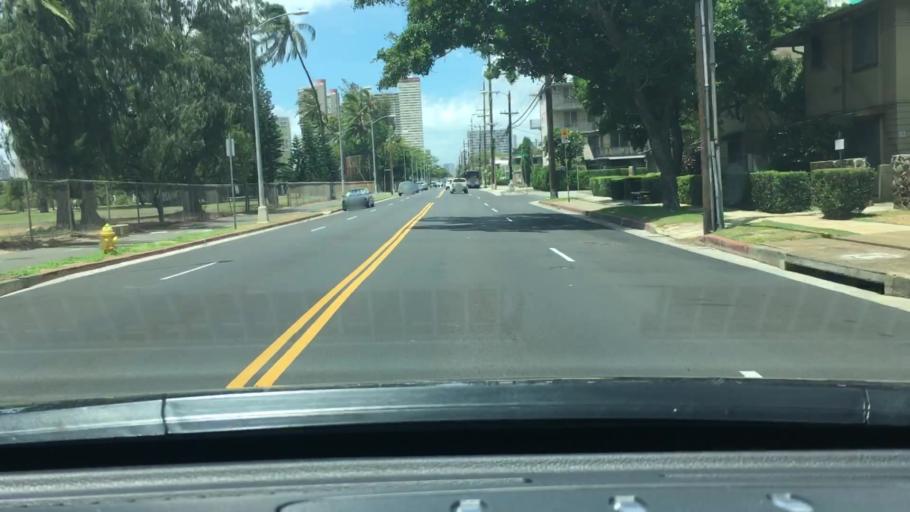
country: US
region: Hawaii
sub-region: Honolulu County
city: Honolulu
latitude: 21.2813
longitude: -157.8164
